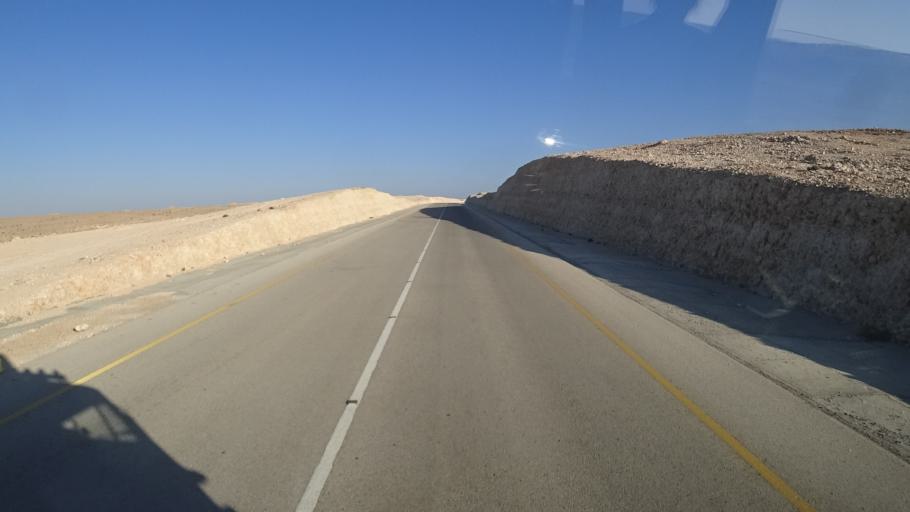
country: YE
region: Al Mahrah
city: Hawf
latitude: 17.0856
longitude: 53.0807
